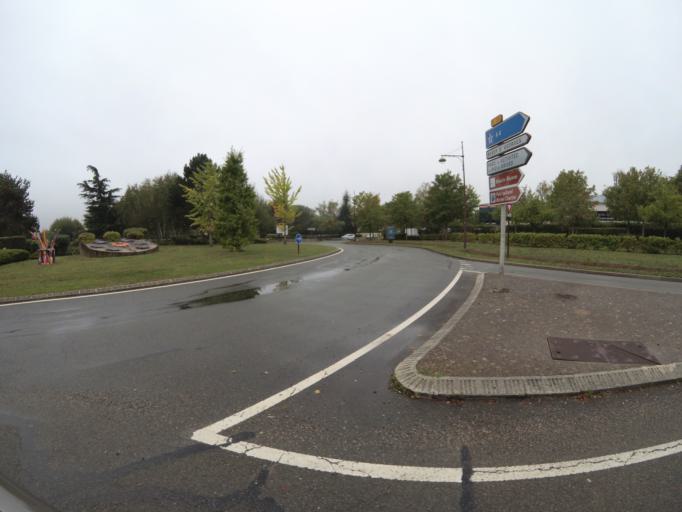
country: FR
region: Ile-de-France
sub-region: Departement de Seine-et-Marne
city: Ferrieres-en-Brie
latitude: 48.8268
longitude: 2.7066
